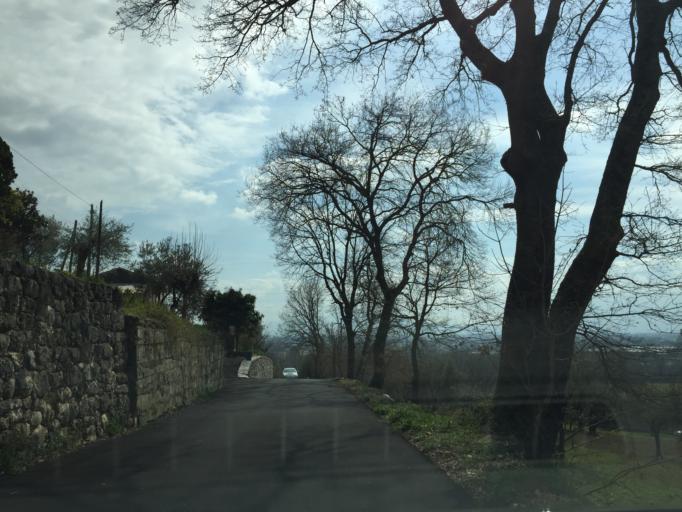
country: IT
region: Latium
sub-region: Provincia di Frosinone
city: Castrocielo
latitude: 41.5221
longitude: 13.7054
